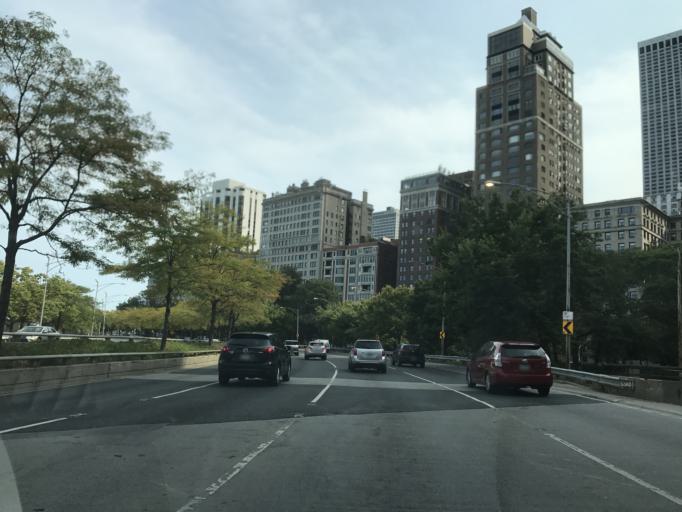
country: US
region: Illinois
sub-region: Cook County
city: Chicago
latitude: 41.9021
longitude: -87.6238
